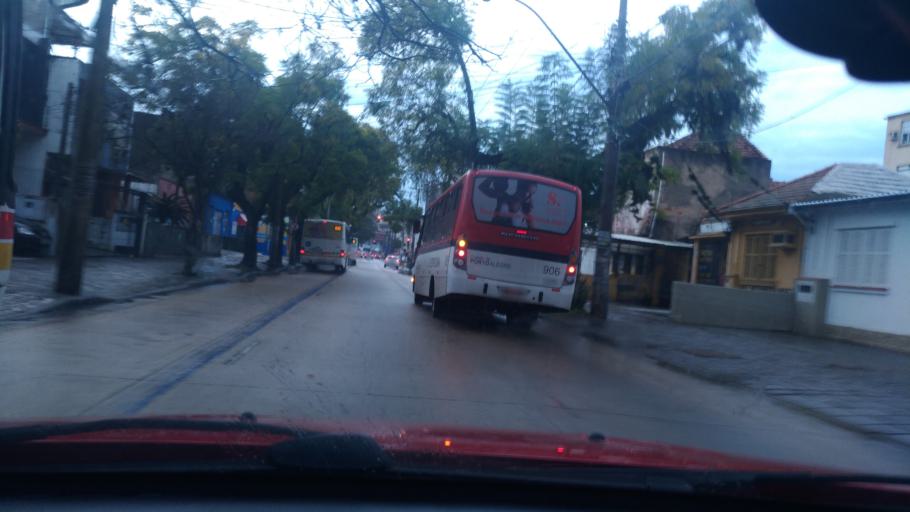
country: BR
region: Rio Grande do Sul
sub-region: Porto Alegre
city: Porto Alegre
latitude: -30.0071
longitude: -51.1948
